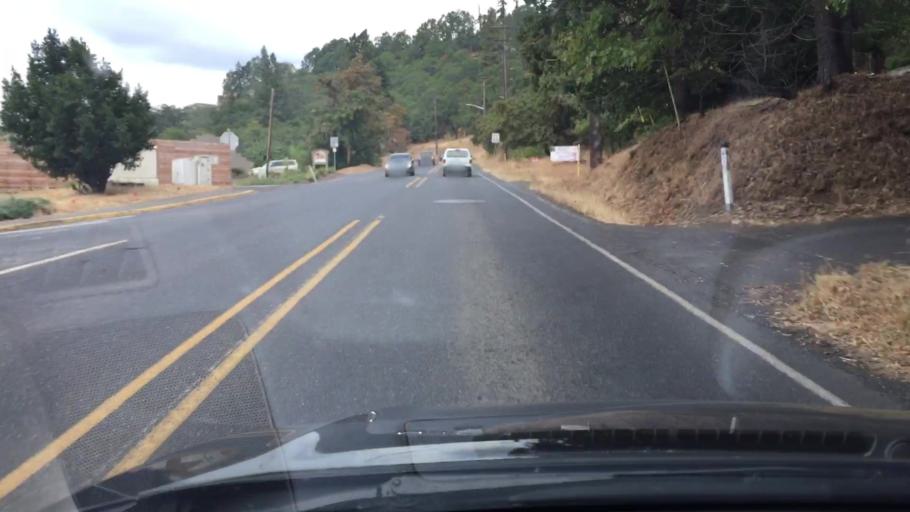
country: US
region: Washington
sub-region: Klickitat County
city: White Salmon
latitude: 45.7175
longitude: -121.4656
